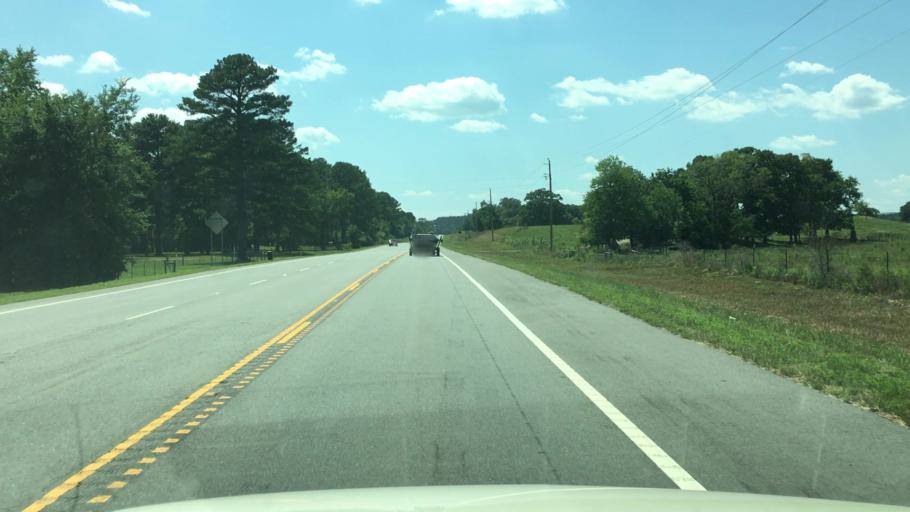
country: US
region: Arkansas
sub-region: Garland County
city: Piney
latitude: 34.5108
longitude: -93.2239
